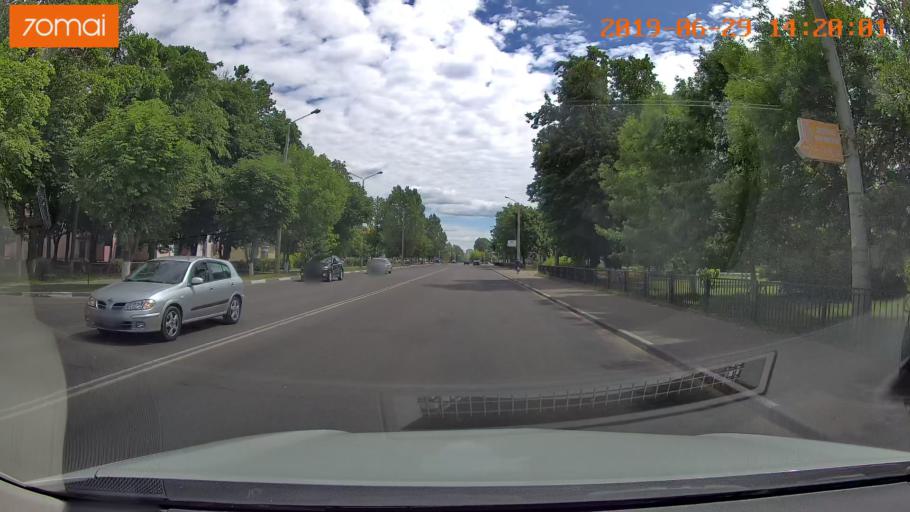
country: BY
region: Minsk
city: Salihorsk
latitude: 52.7948
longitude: 27.5411
